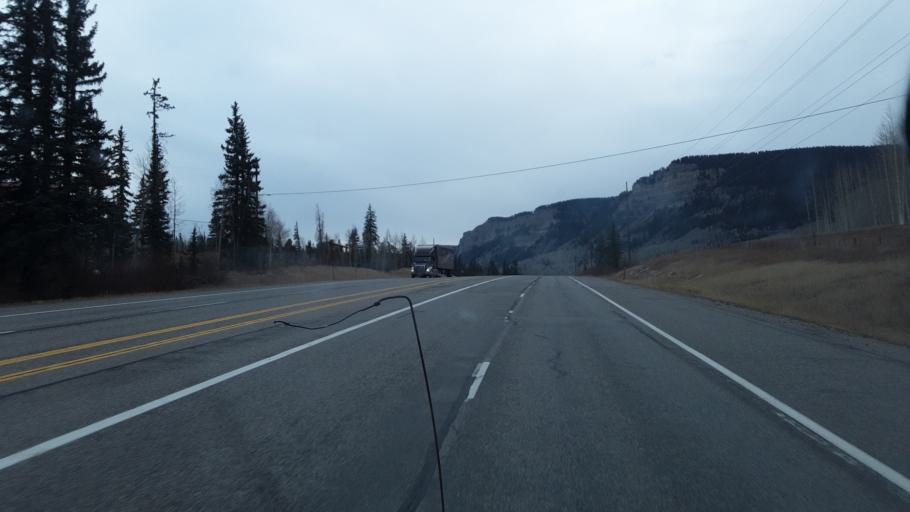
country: US
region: Colorado
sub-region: San Juan County
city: Silverton
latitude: 37.6100
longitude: -107.8145
